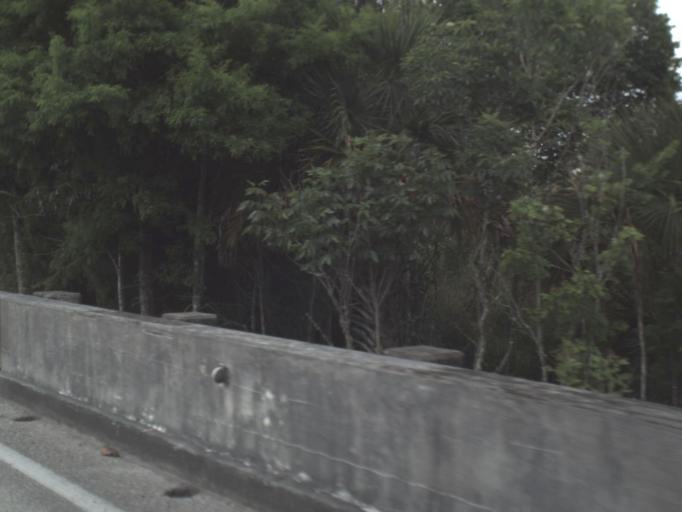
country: US
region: Florida
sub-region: Flagler County
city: Palm Coast
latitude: 29.6512
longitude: -81.2869
